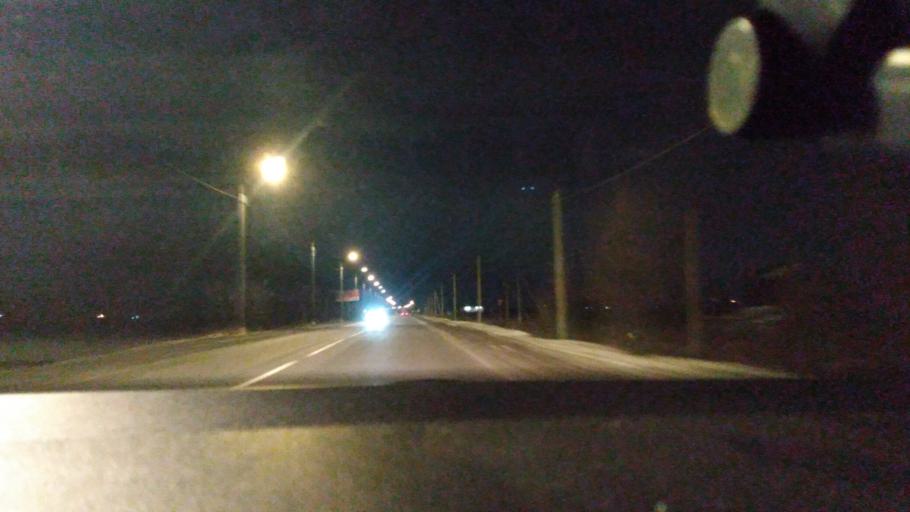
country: RU
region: Moskovskaya
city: Yegor'yevsk
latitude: 55.4081
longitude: 39.0528
